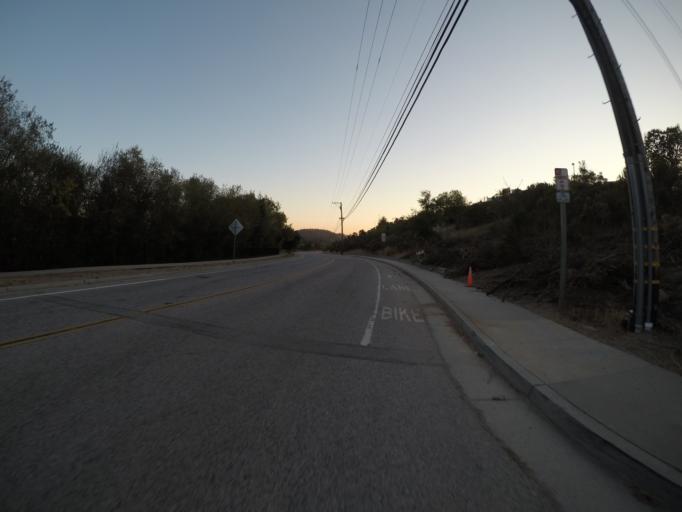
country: US
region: California
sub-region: Santa Cruz County
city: Scotts Valley
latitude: 37.0729
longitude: -122.0045
